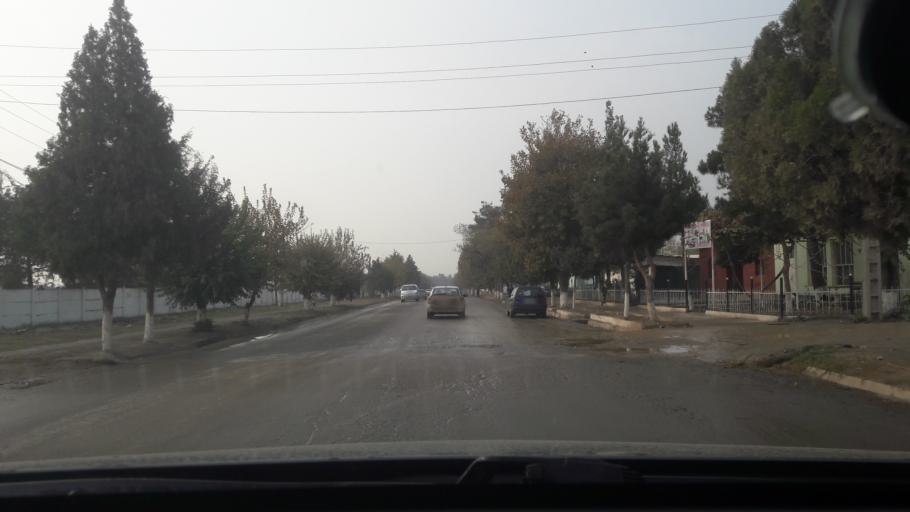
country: TJ
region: Khatlon
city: Abdurahmoni Jomi
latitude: 37.9849
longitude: 68.7007
